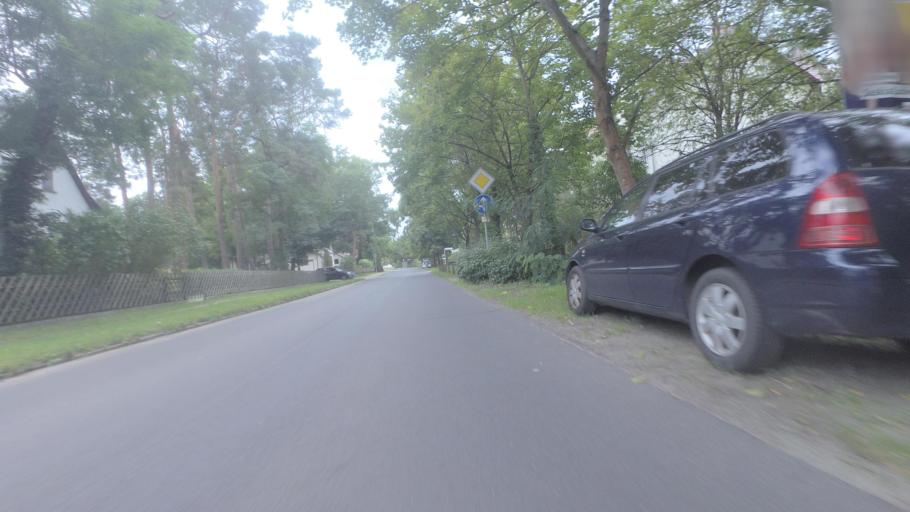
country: DE
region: Brandenburg
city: Potsdam
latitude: 52.3457
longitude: 13.1036
